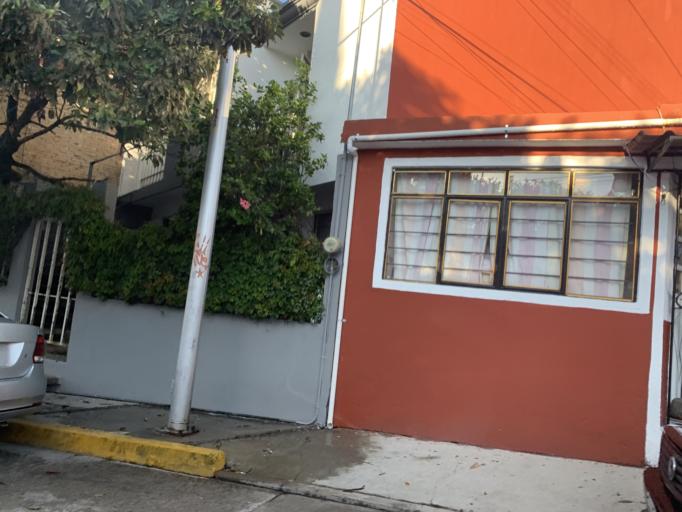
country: MX
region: Puebla
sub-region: San Pedro Cholula
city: Santiago Momoxpan
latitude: 19.0737
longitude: -98.2458
